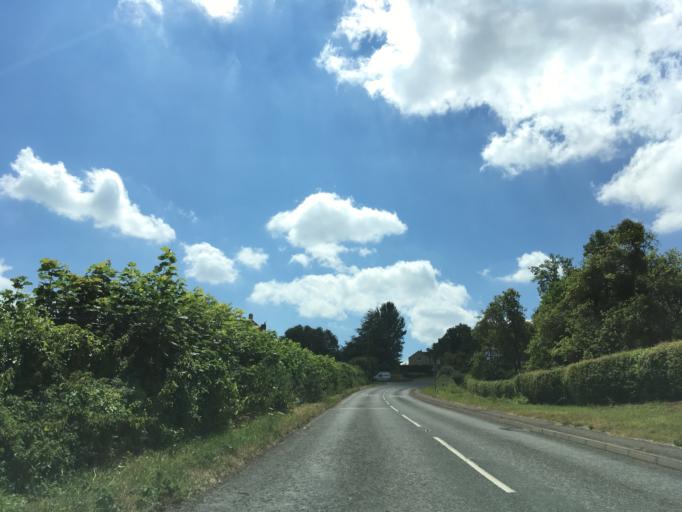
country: GB
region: England
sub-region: Gloucestershire
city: Barnwood
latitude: 51.8286
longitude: -2.2058
